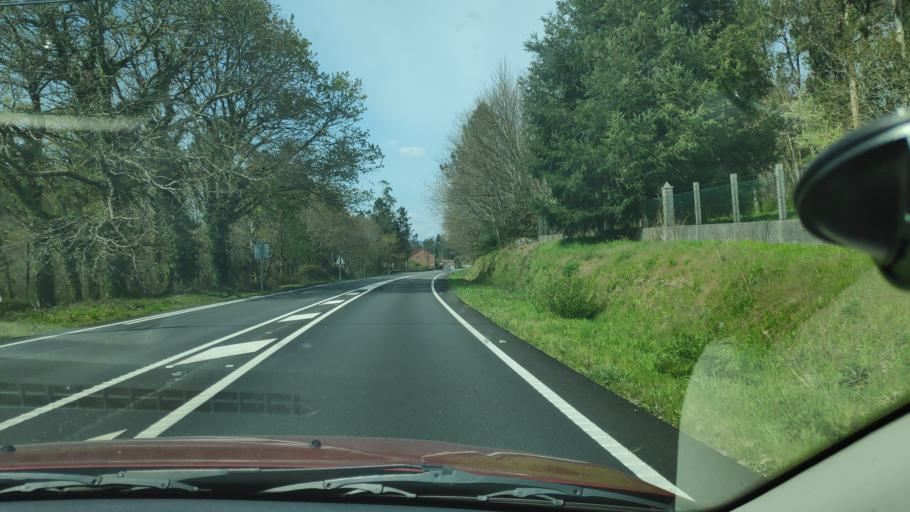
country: ES
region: Galicia
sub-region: Provincia da Coruna
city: Ames
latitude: 42.8865
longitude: -8.6842
